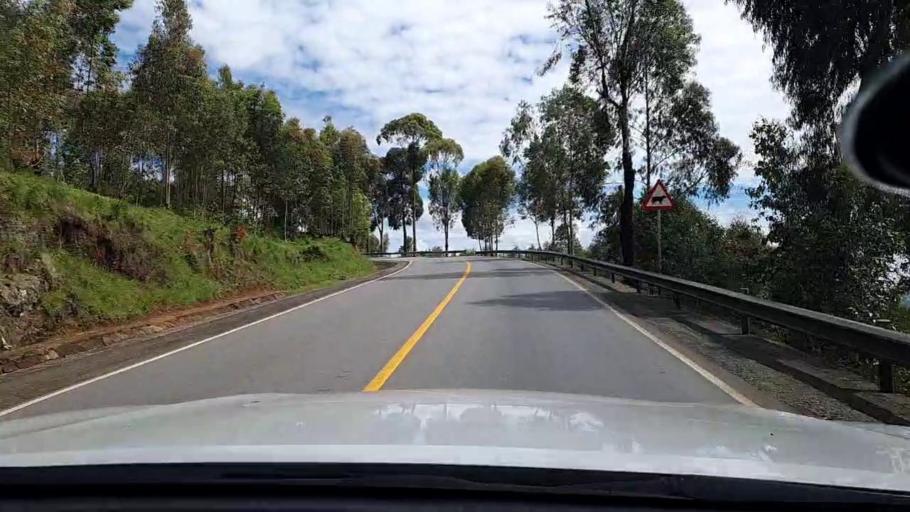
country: RW
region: Kigali
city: Kigali
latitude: -1.8253
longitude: 29.9479
